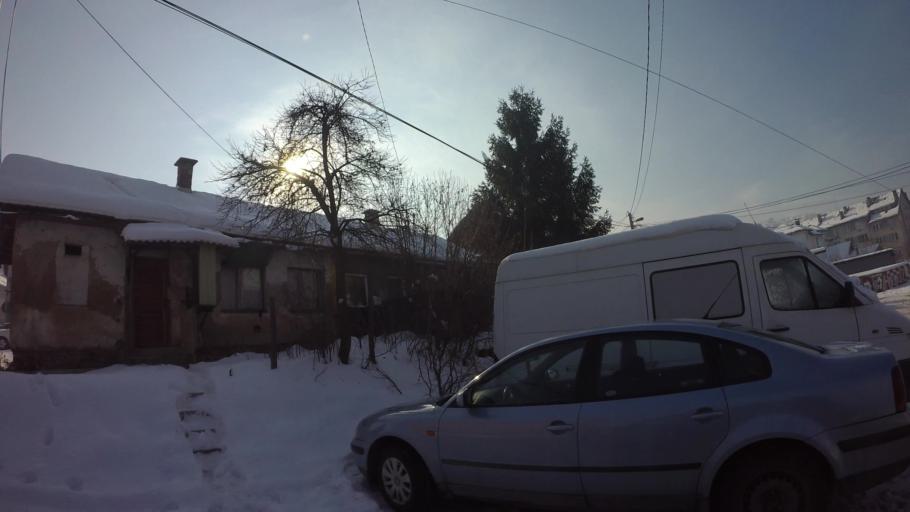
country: BA
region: Federation of Bosnia and Herzegovina
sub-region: Kanton Sarajevo
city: Sarajevo
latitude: 43.8430
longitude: 18.3643
